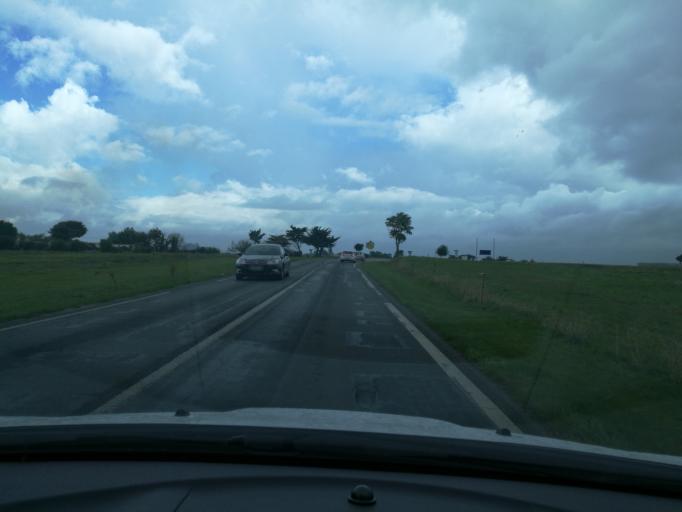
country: FR
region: Poitou-Charentes
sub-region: Departement de la Charente-Maritime
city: Saint-Martin-de-Re
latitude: 46.2001
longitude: -1.3737
